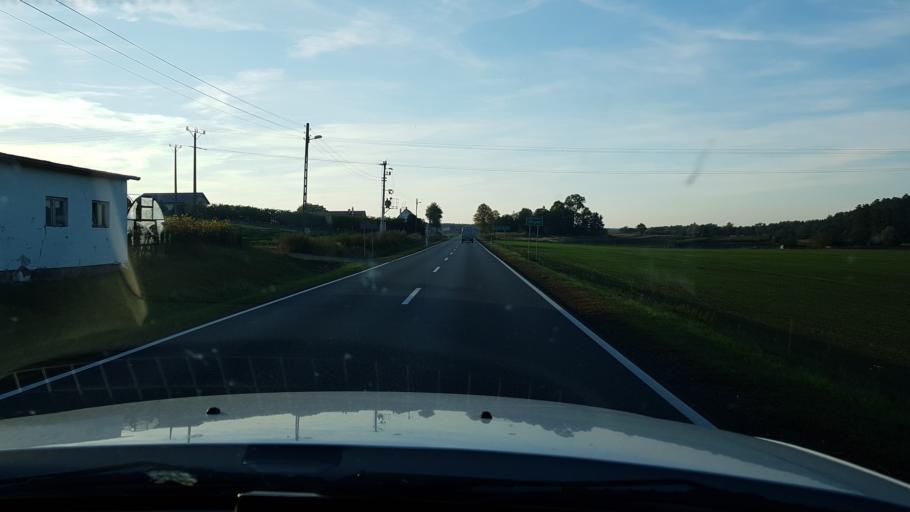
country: PL
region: West Pomeranian Voivodeship
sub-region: Powiat gryfinski
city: Chojna
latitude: 52.9638
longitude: 14.4079
